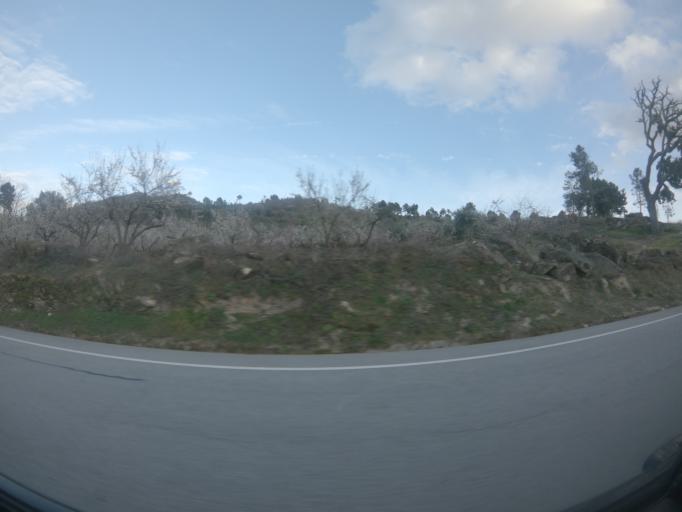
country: PT
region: Braganca
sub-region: Carrazeda de Ansiaes
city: Carrazeda de Anciaes
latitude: 41.2660
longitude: -7.3242
